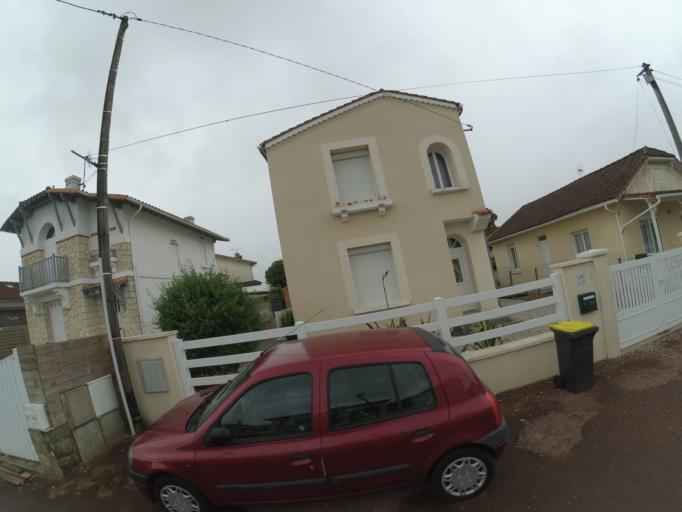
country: FR
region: Poitou-Charentes
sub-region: Departement de la Charente-Maritime
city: Saint-Georges-de-Didonne
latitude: 45.6218
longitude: -1.0094
